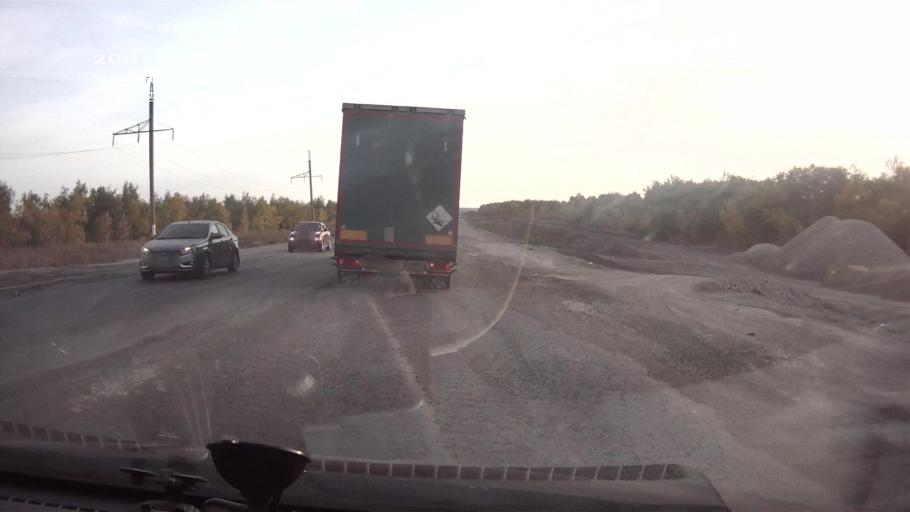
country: RU
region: Saratov
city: Krasnyy Oktyabr'
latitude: 51.3047
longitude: 45.6928
